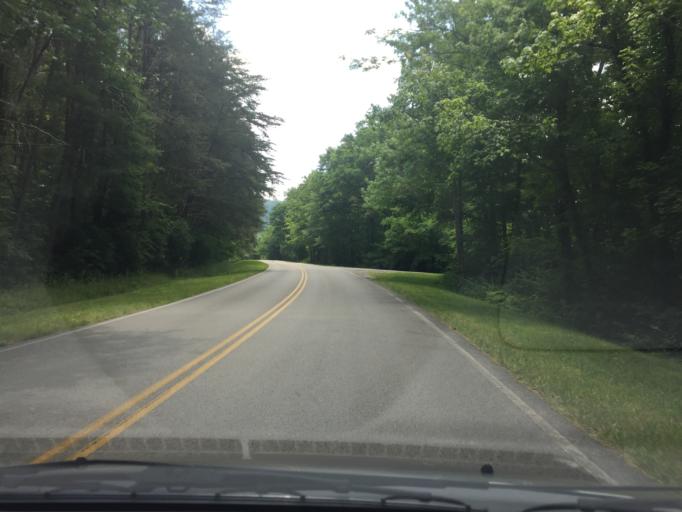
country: US
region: Tennessee
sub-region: Hamilton County
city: Lookout Mountain
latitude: 35.0478
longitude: -85.4254
